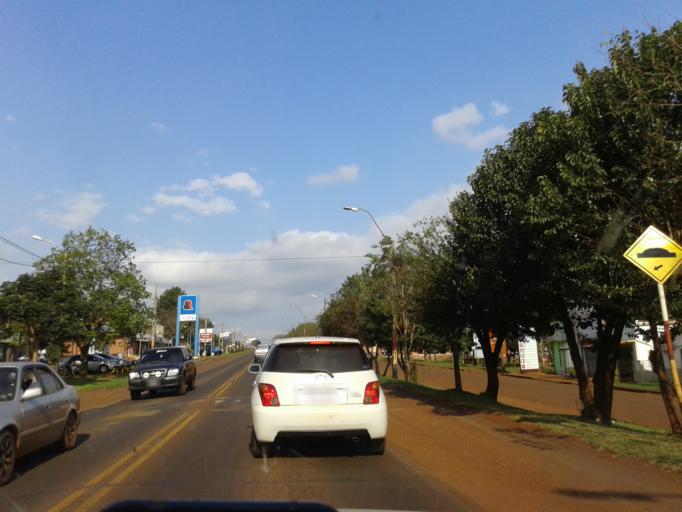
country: PY
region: Itapua
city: Arquitecto Tomas Romero Pereira
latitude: -26.5221
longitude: -55.2664
